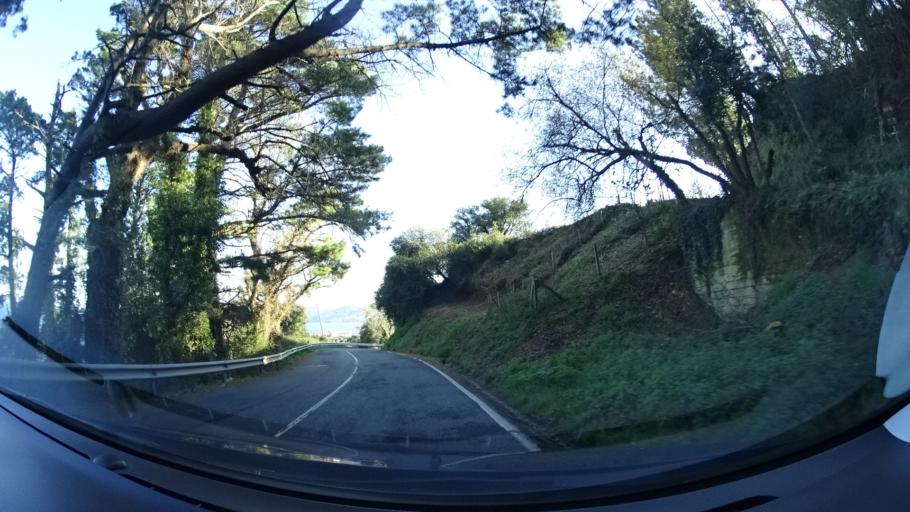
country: ES
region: Basque Country
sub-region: Bizkaia
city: Bermeo
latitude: 43.4283
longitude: -2.7414
